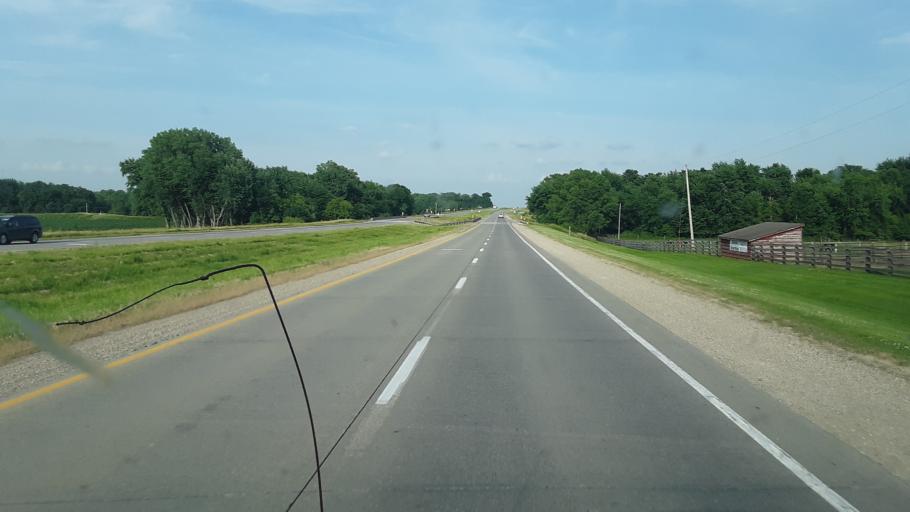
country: US
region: Iowa
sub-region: Marshall County
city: Marshalltown
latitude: 42.0069
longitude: -92.8570
